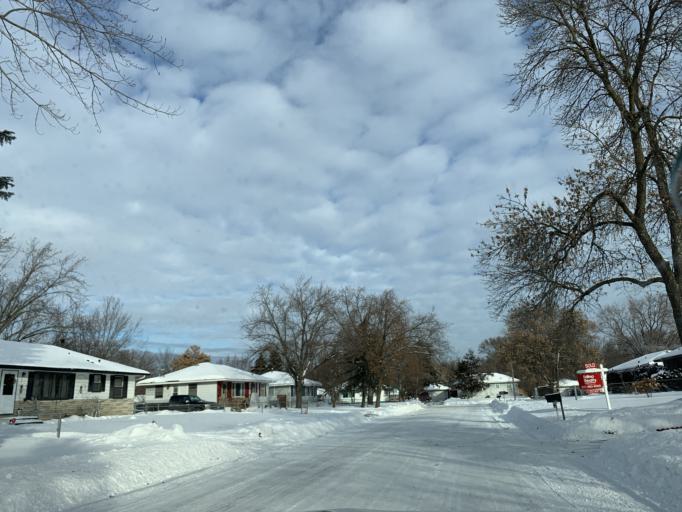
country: US
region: Minnesota
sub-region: Anoka County
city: Coon Rapids
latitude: 45.1699
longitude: -93.2871
